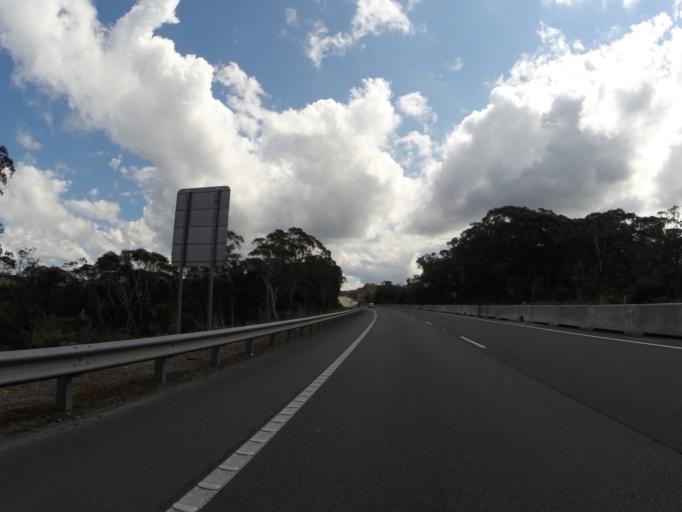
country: AU
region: New South Wales
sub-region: Wollongong
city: Mount Keira
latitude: -34.3705
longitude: 150.8282
